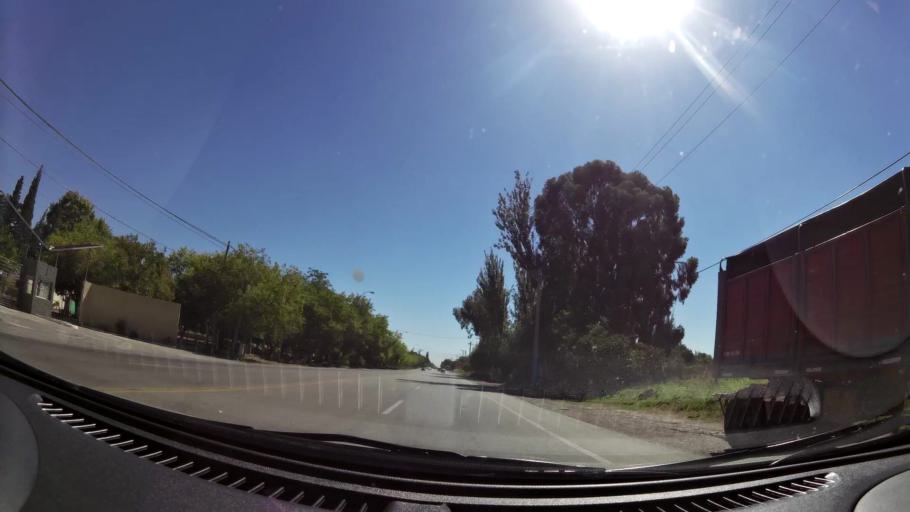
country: AR
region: San Juan
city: Villa Krause
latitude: -31.6040
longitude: -68.5433
